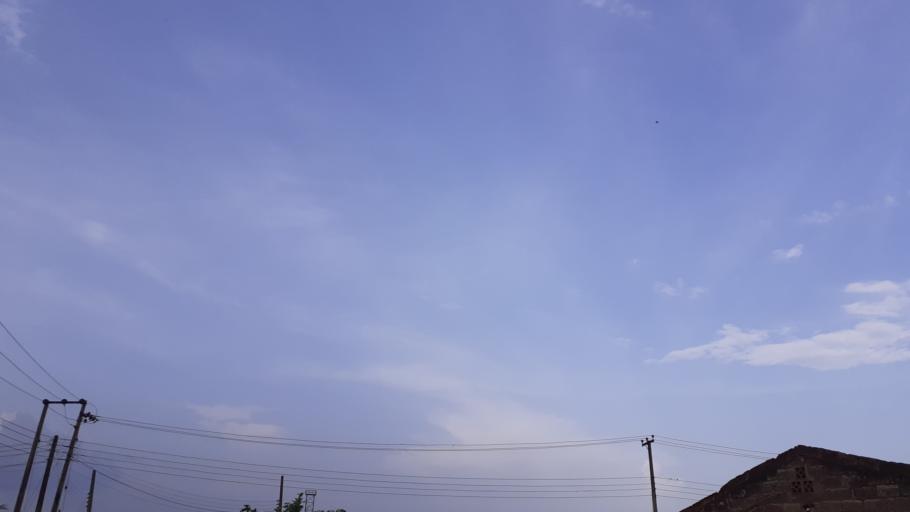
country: NG
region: Ondo
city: Akure
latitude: 7.2138
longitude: 5.2172
